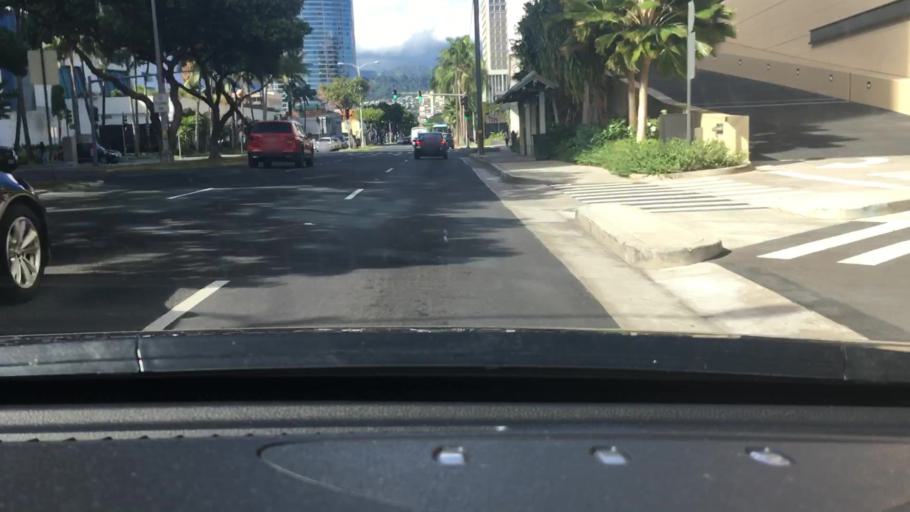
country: US
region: Hawaii
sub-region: Honolulu County
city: Honolulu
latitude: 21.2914
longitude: -157.8475
